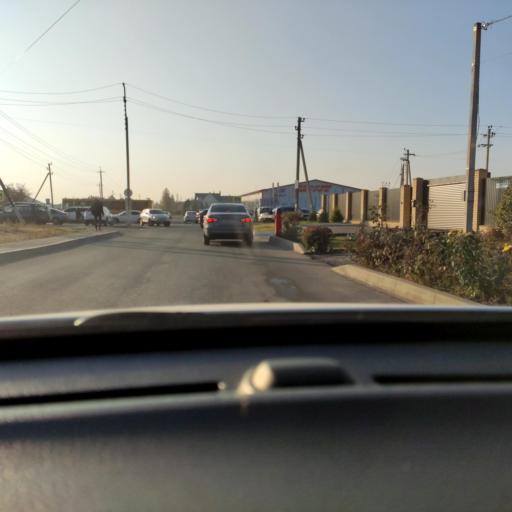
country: RU
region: Voronezj
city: Somovo
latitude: 51.6850
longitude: 39.3212
